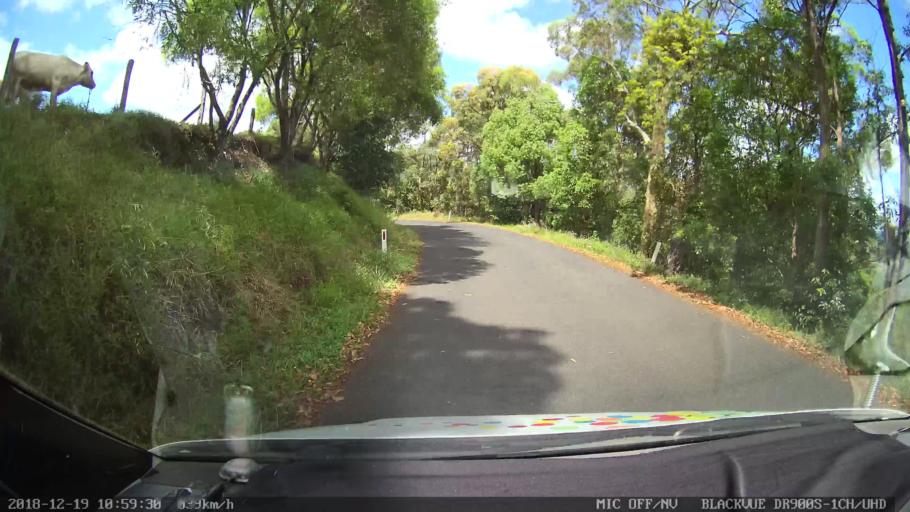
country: AU
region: New South Wales
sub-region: Lismore Municipality
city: Nimbin
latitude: -28.5965
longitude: 153.2619
